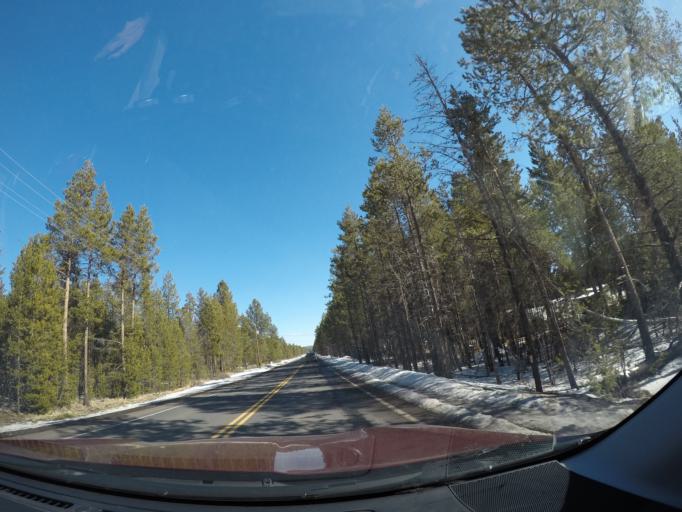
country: US
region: Oregon
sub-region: Deschutes County
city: Sunriver
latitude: 43.8629
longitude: -121.4721
